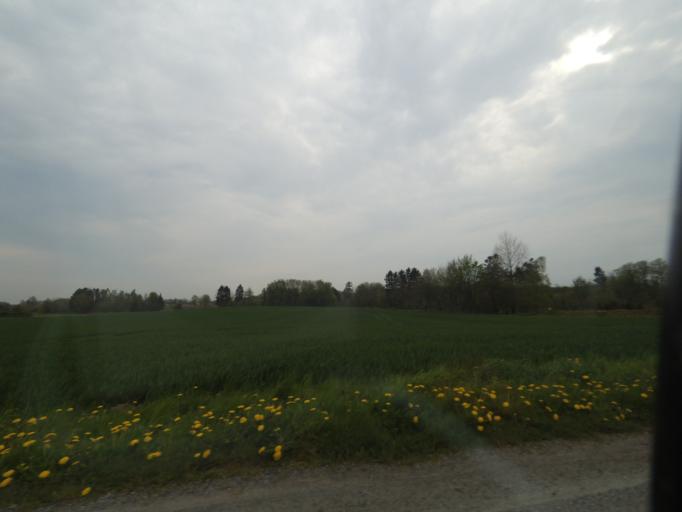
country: DK
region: South Denmark
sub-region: Faaborg-Midtfyn Kommune
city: Ringe
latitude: 55.1854
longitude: 10.5778
